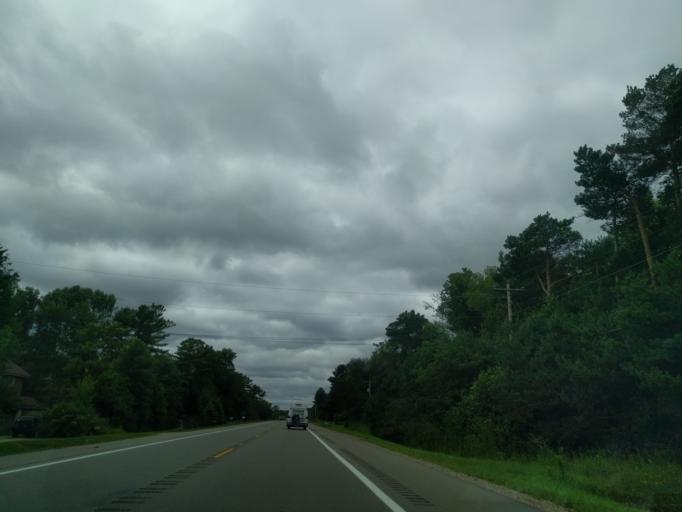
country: US
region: Michigan
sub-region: Menominee County
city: Menominee
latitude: 45.1906
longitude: -87.5524
